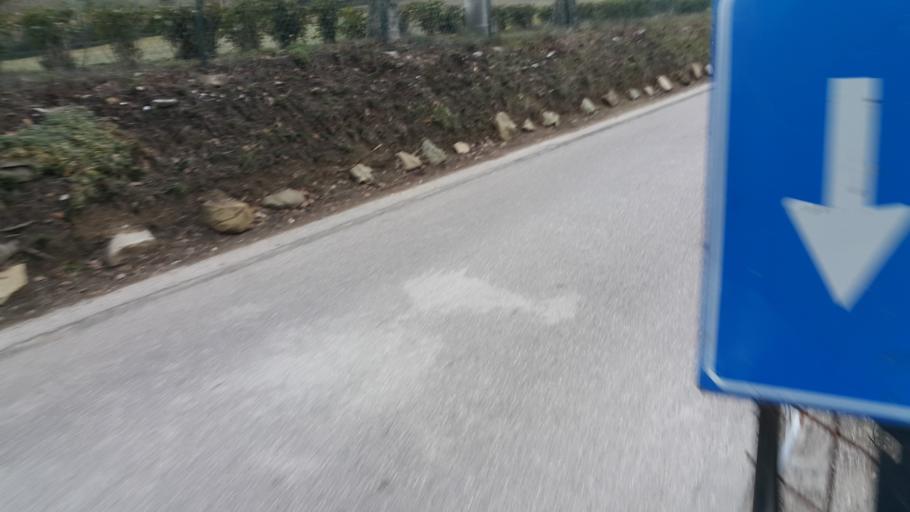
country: IT
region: Umbria
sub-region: Provincia di Perugia
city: Perugia
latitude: 43.0911
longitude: 12.3770
